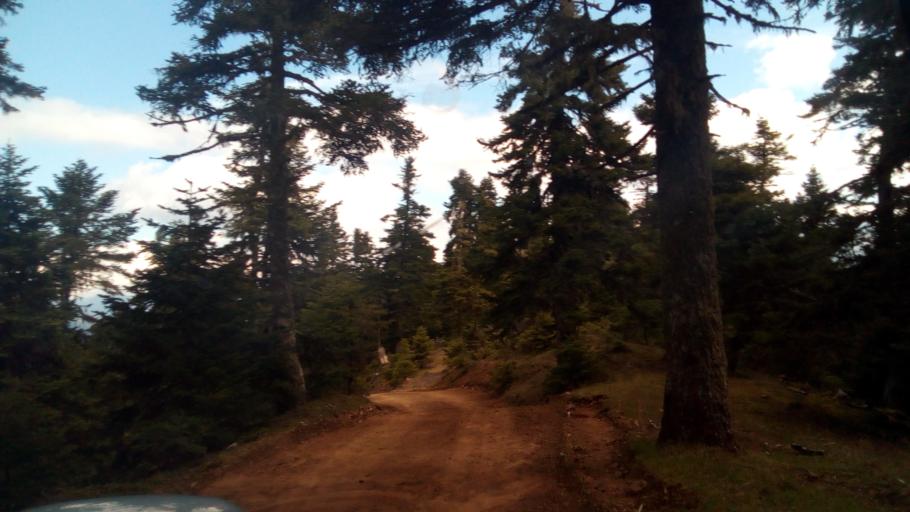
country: GR
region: Central Greece
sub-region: Nomos Fokidos
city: Lidoriki
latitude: 38.6128
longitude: 21.9720
